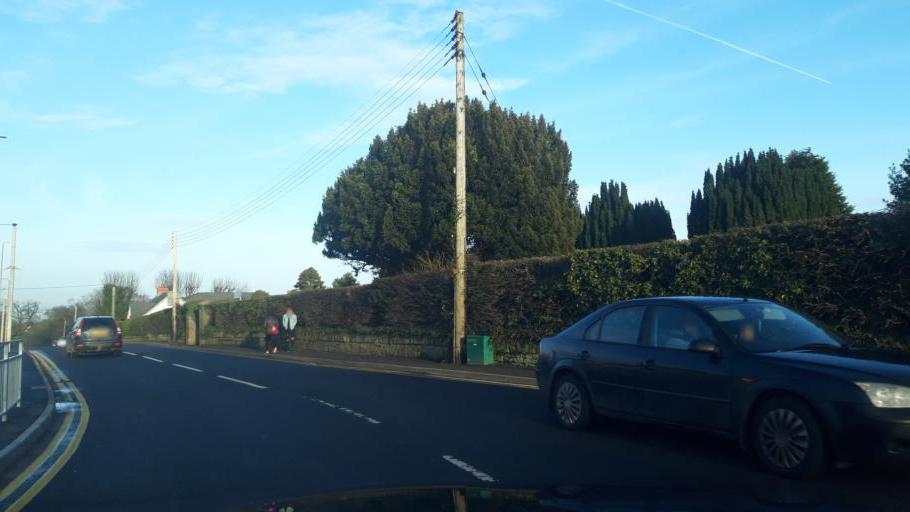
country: GB
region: Northern Ireland
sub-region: Dungannon District
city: Dungannon
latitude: 54.5088
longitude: -6.7667
